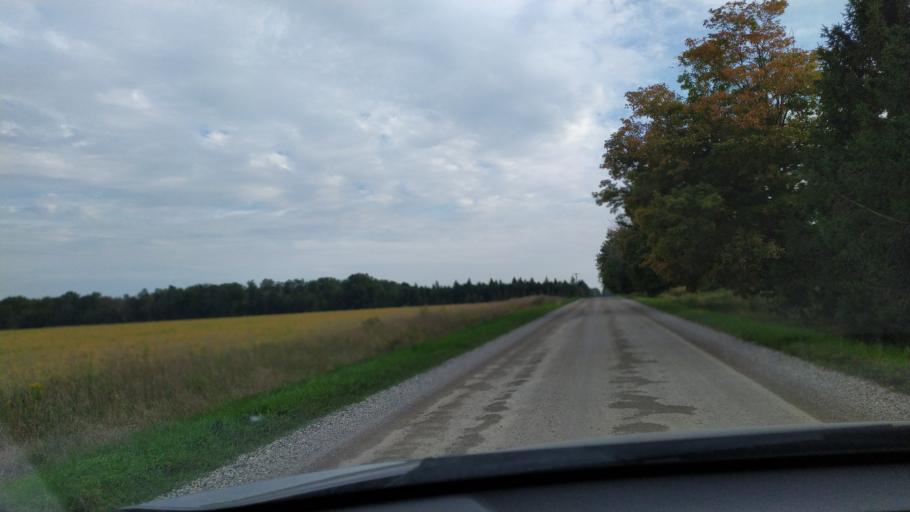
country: CA
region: Ontario
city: Stratford
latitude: 43.4104
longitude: -80.9131
